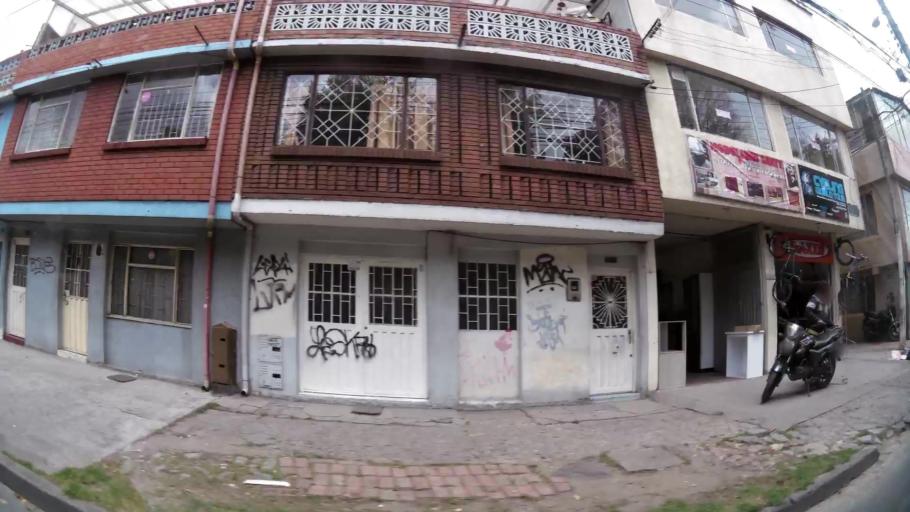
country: CO
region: Cundinamarca
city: Funza
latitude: 4.7122
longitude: -74.1157
